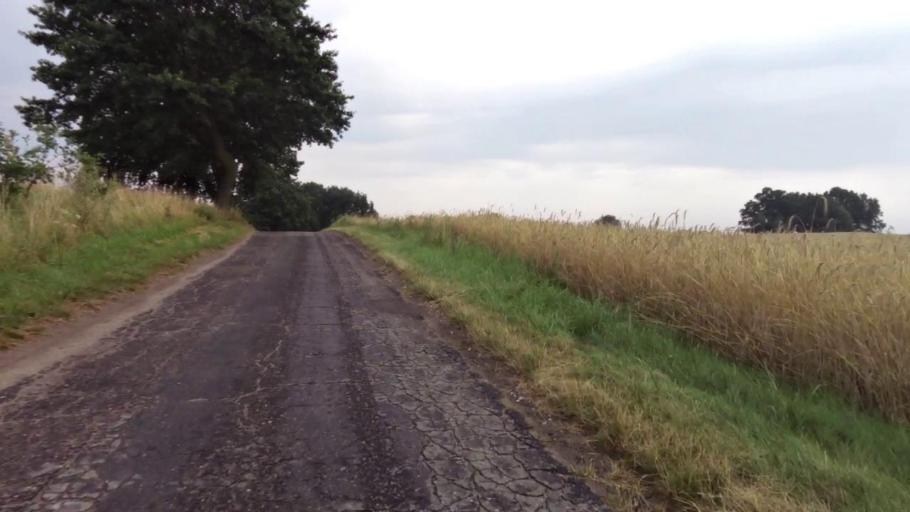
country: PL
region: West Pomeranian Voivodeship
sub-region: Powiat drawski
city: Drawsko Pomorskie
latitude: 53.5377
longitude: 15.7257
